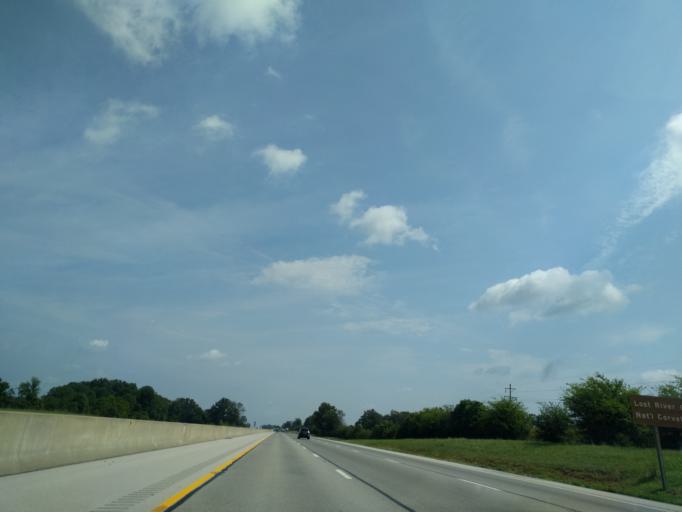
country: US
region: Kentucky
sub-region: Warren County
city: Plano
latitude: 36.8775
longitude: -86.4462
